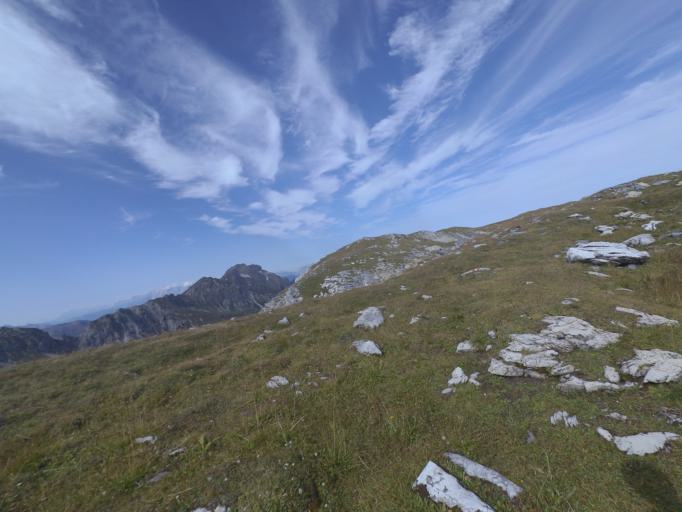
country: AT
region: Salzburg
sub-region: Politischer Bezirk Sankt Johann im Pongau
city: Kleinarl
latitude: 47.2229
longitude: 13.3891
